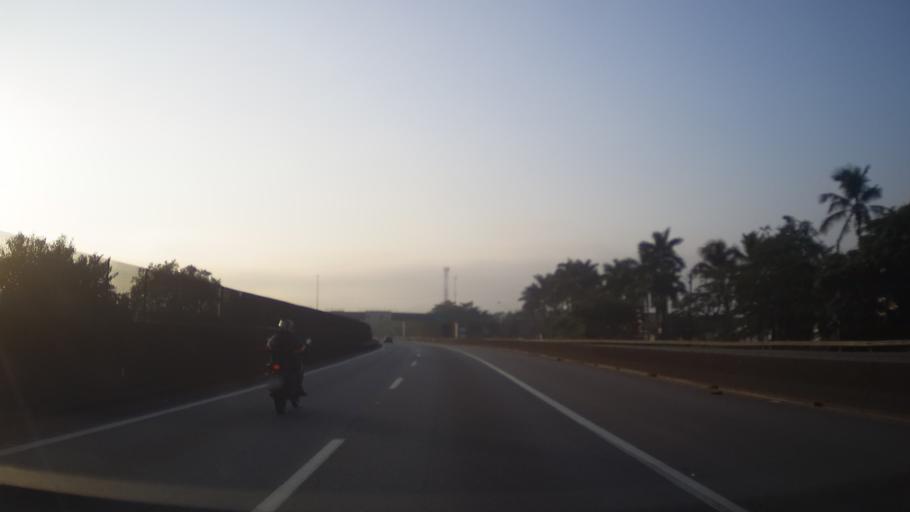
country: BR
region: Sao Paulo
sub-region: Cubatao
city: Cubatao
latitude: -23.9264
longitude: -46.4061
